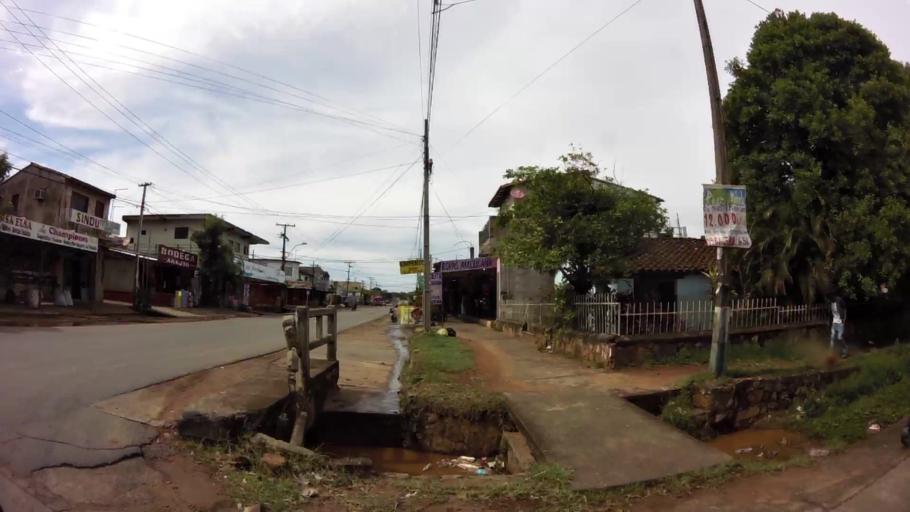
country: PY
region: Central
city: Limpio
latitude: -25.1710
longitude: -57.4733
